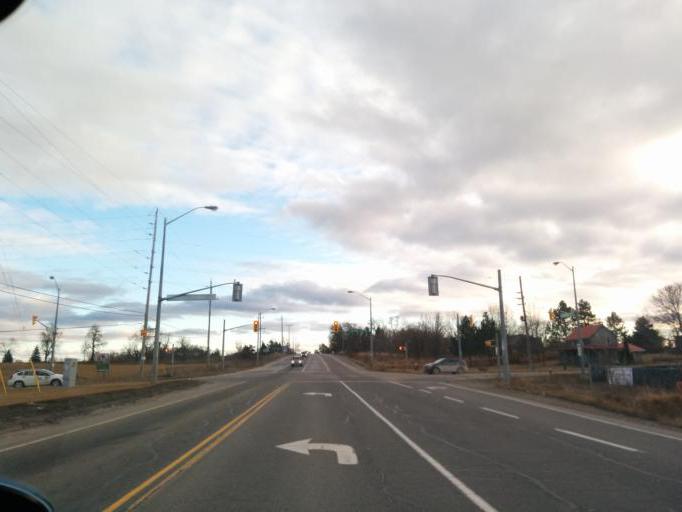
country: CA
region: Ontario
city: Bradford West Gwillimbury
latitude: 43.9933
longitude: -79.6744
